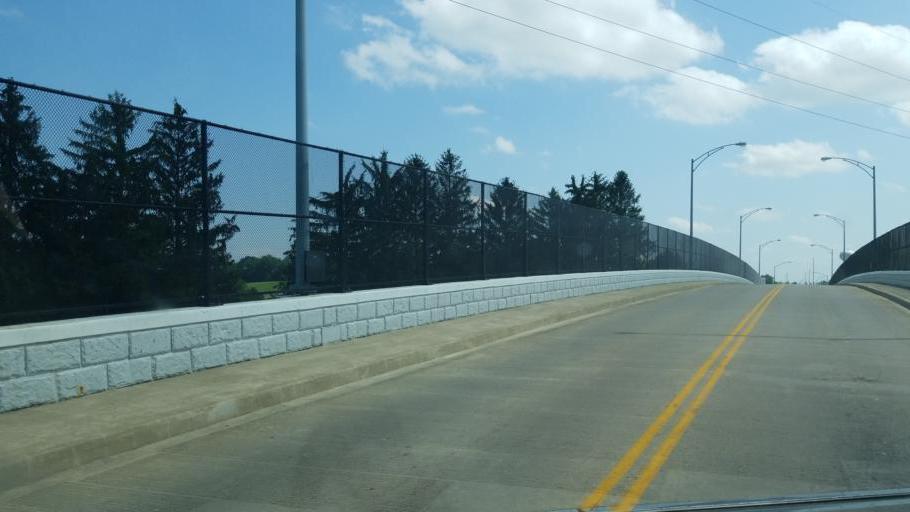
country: US
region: Ohio
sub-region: Huron County
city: Bellevue
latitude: 41.2656
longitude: -82.8402
